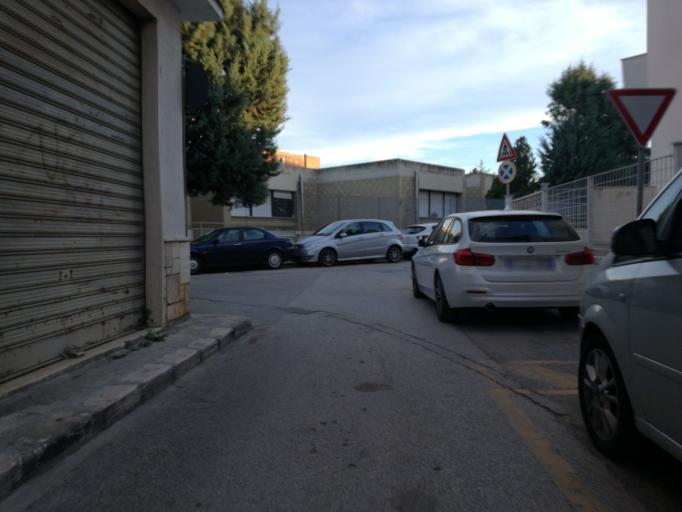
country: IT
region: Apulia
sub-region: Provincia di Bari
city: Valenzano
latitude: 41.0392
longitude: 16.8827
